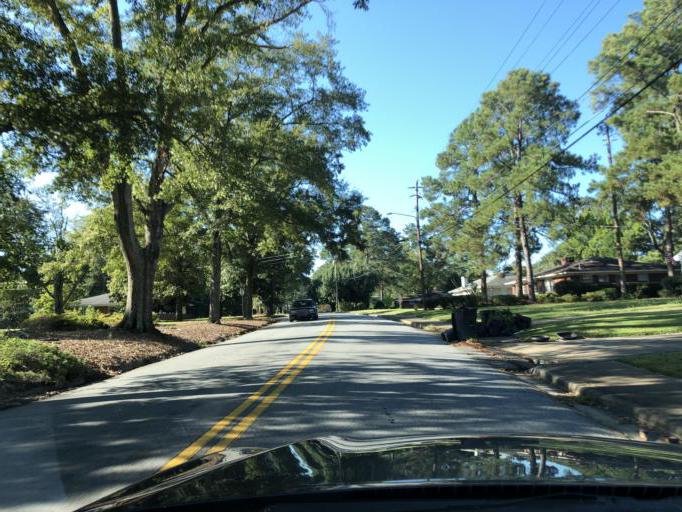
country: US
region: Georgia
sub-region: Muscogee County
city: Columbus
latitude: 32.4898
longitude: -84.9455
